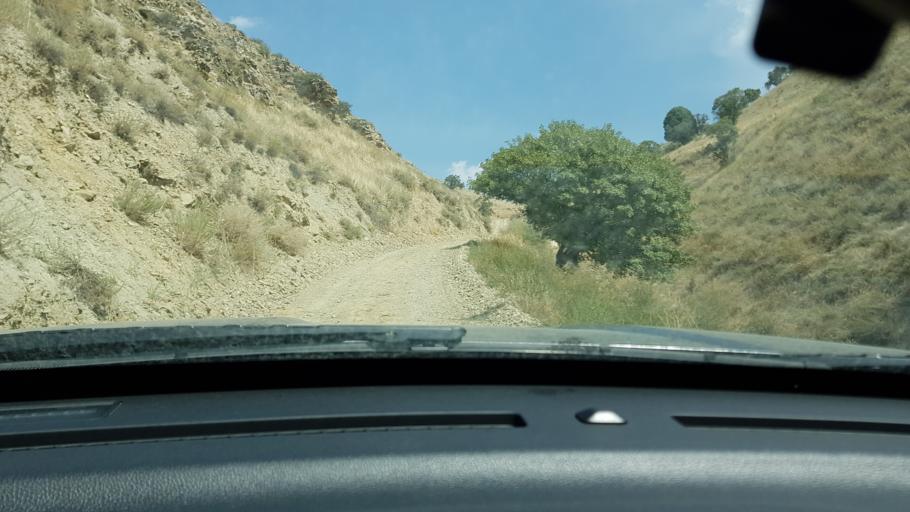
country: TM
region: Ahal
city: Baharly
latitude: 38.4043
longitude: 56.9057
